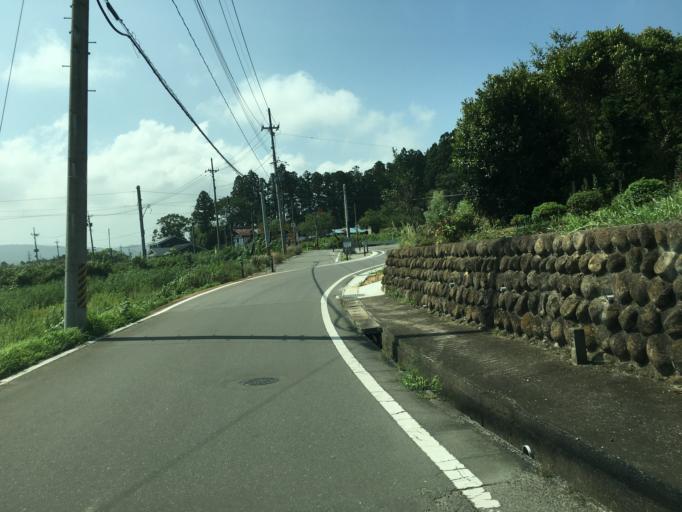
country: JP
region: Miyagi
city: Marumori
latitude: 37.8324
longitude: 140.9261
